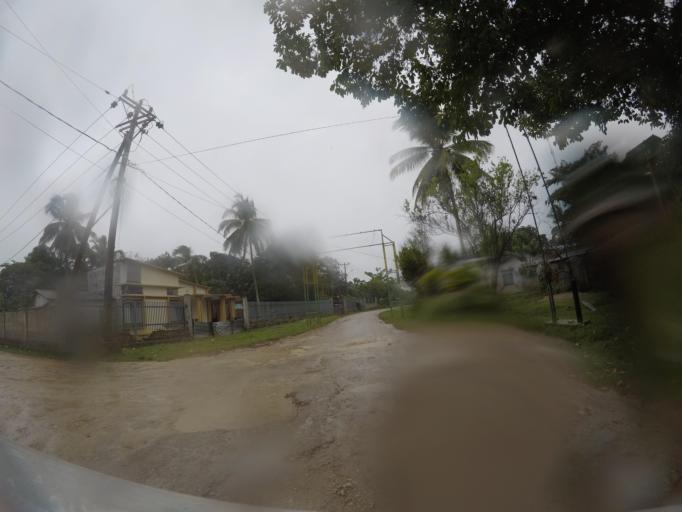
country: TL
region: Lautem
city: Lospalos
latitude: -8.5195
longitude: 127.0043
